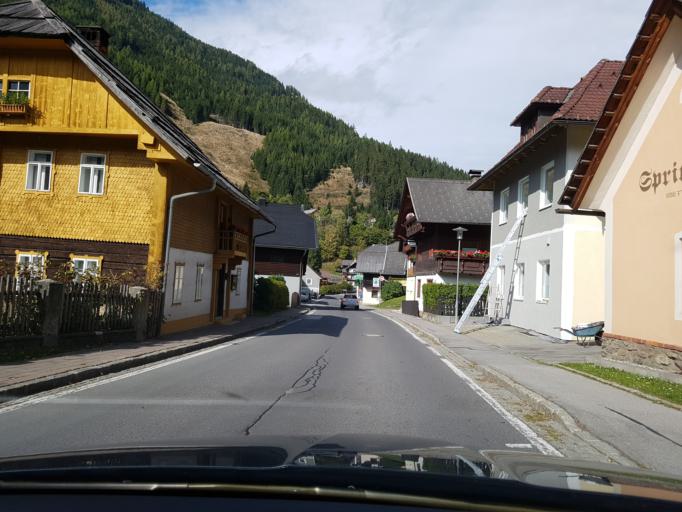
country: AT
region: Carinthia
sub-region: Politischer Bezirk Feldkirchen
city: Gnesau
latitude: 46.8549
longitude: 13.8932
